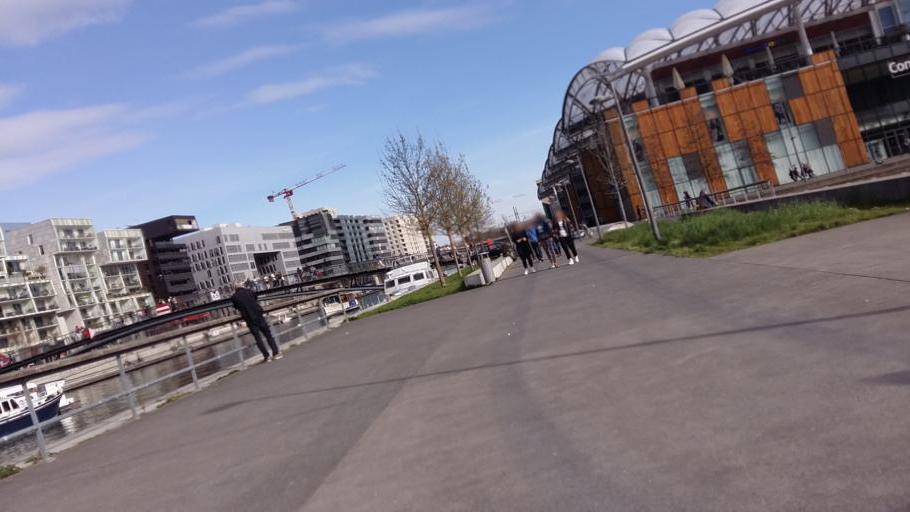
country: FR
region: Rhone-Alpes
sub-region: Departement du Rhone
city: La Mulatiere
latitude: 45.7424
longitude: 4.8150
